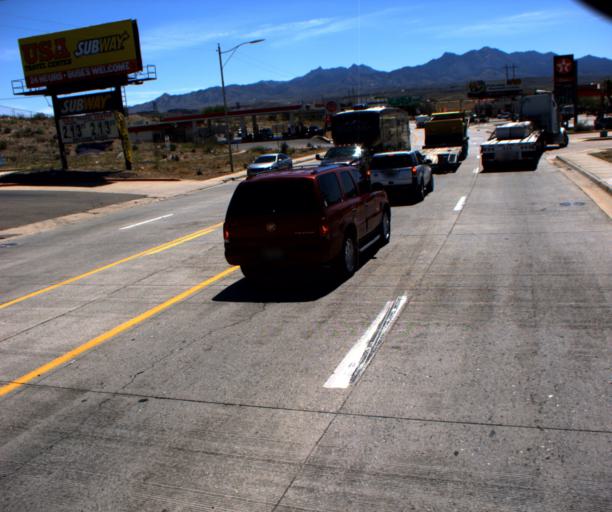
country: US
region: Arizona
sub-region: Mohave County
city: Kingman
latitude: 35.1922
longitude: -114.0707
